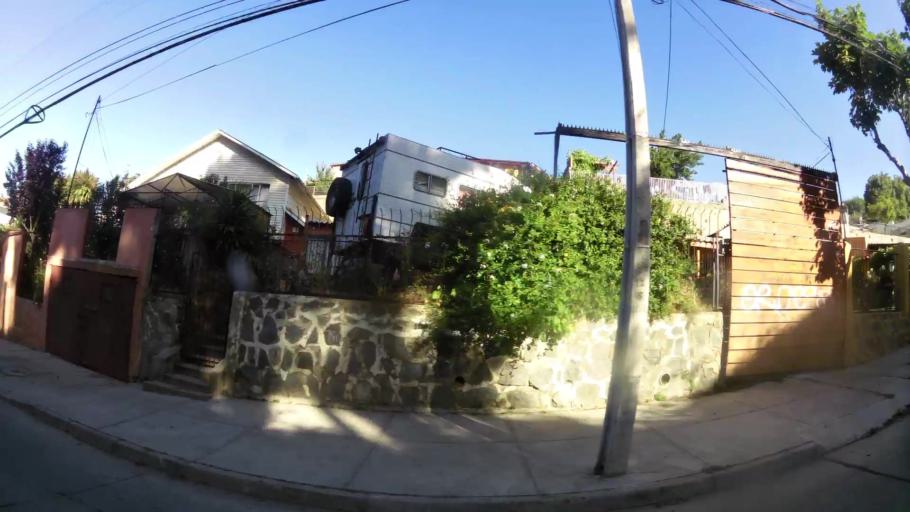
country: CL
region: Valparaiso
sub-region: Provincia de Valparaiso
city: Vina del Mar
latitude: -33.0328
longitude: -71.5642
